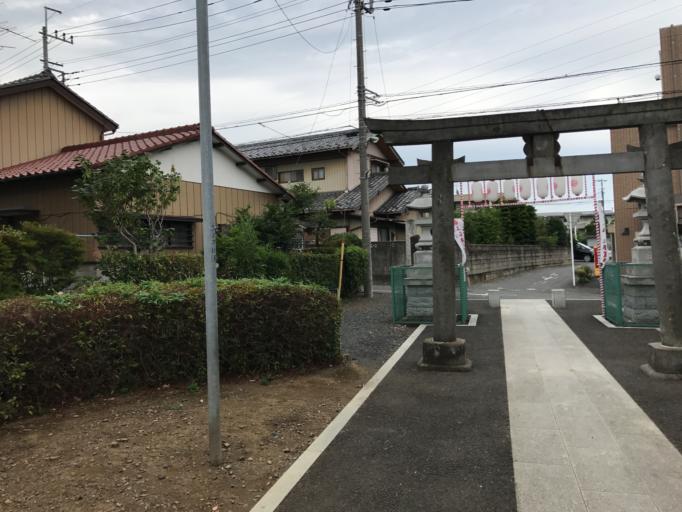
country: JP
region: Saitama
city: Yono
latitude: 35.8874
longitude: 139.6472
